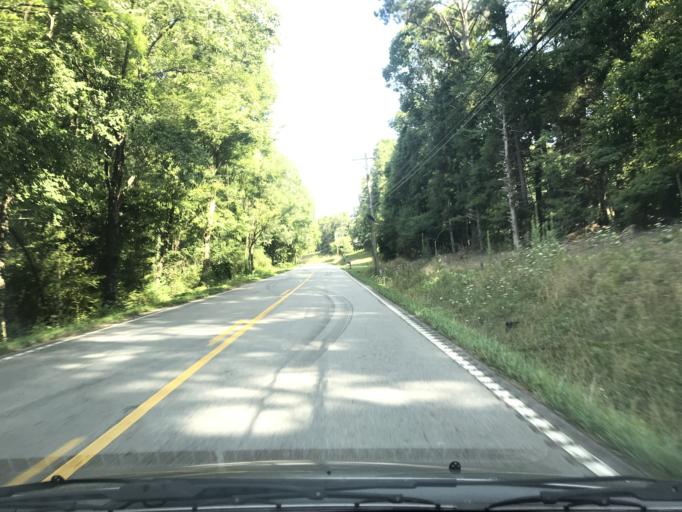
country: US
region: Tennessee
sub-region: Hamilton County
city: Lakesite
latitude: 35.2278
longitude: -85.0611
